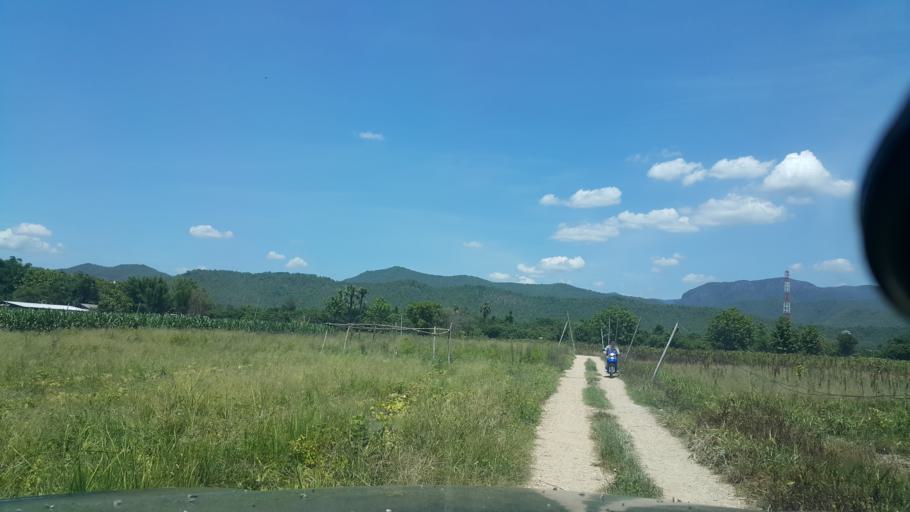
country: TH
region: Chiang Mai
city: San Kamphaeng
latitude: 18.6998
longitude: 99.1544
